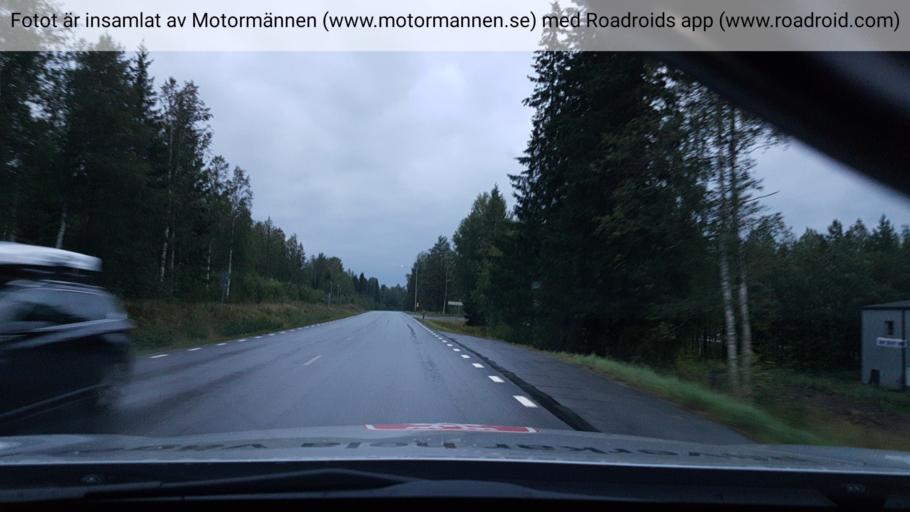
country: SE
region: Vaesterbotten
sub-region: Umea Kommun
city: Ersmark
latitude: 63.8625
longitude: 20.3006
